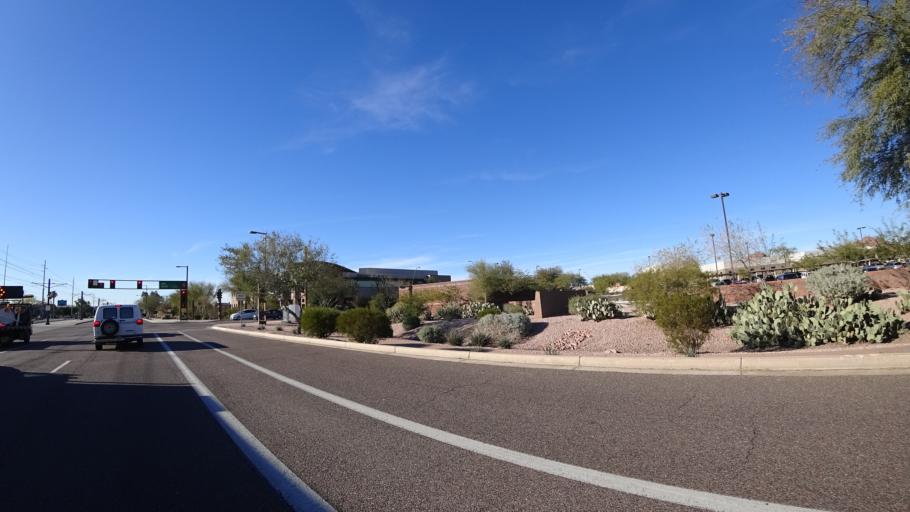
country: US
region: Arizona
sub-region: Maricopa County
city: Tempe Junction
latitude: 33.4453
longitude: -111.9606
